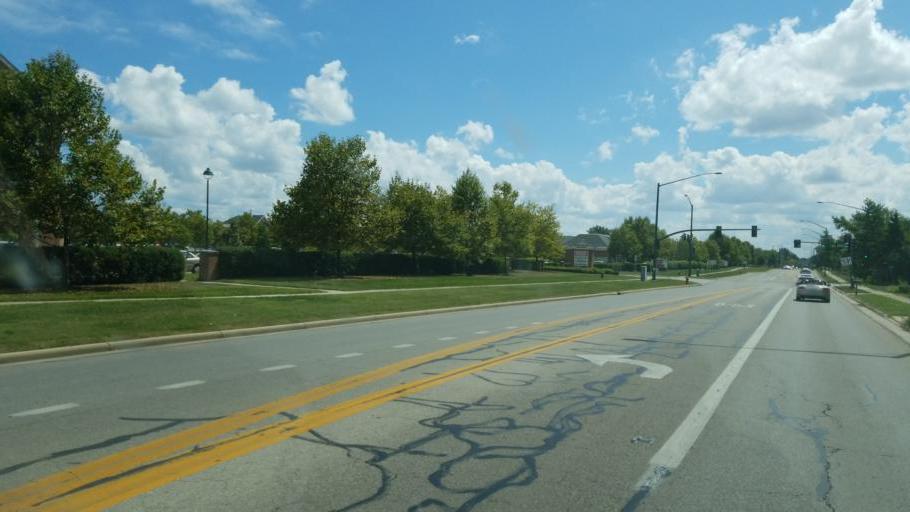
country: US
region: Ohio
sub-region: Franklin County
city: Westerville
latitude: 40.1458
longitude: -82.9246
